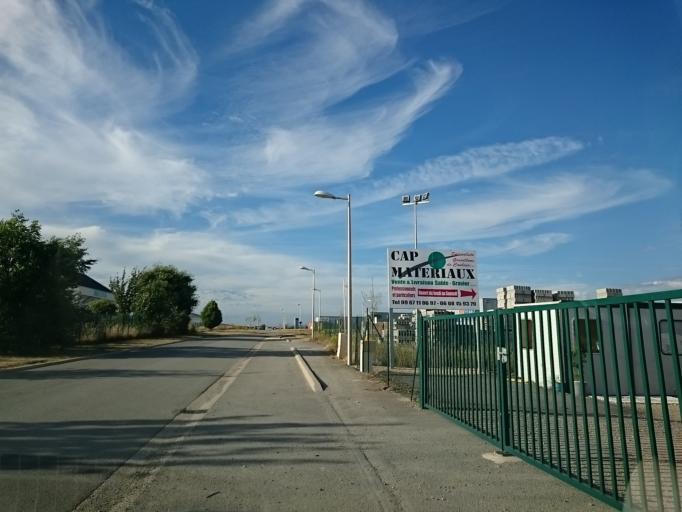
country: FR
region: Brittany
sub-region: Departement d'Ille-et-Vilaine
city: Bain-de-Bretagne
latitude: 47.8554
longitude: -1.6818
